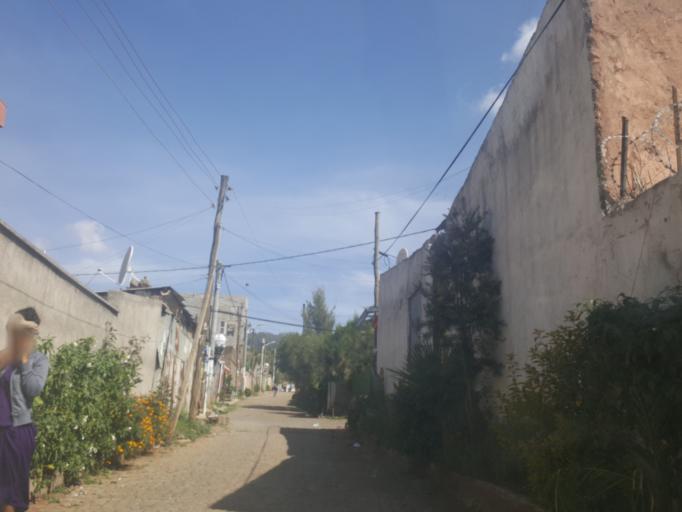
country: ET
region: Adis Abeba
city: Addis Ababa
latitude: 9.0650
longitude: 38.7255
